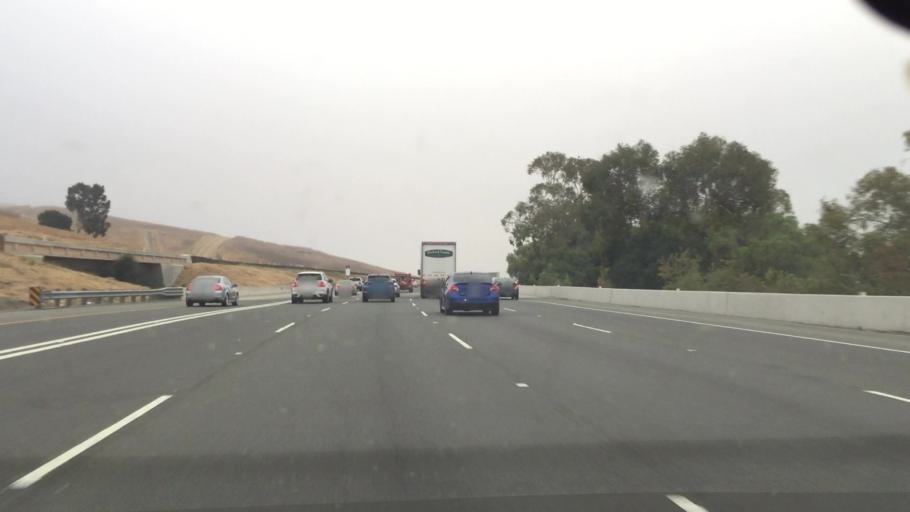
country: US
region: California
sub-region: Santa Clara County
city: Milpitas
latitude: 37.4849
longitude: -121.9148
